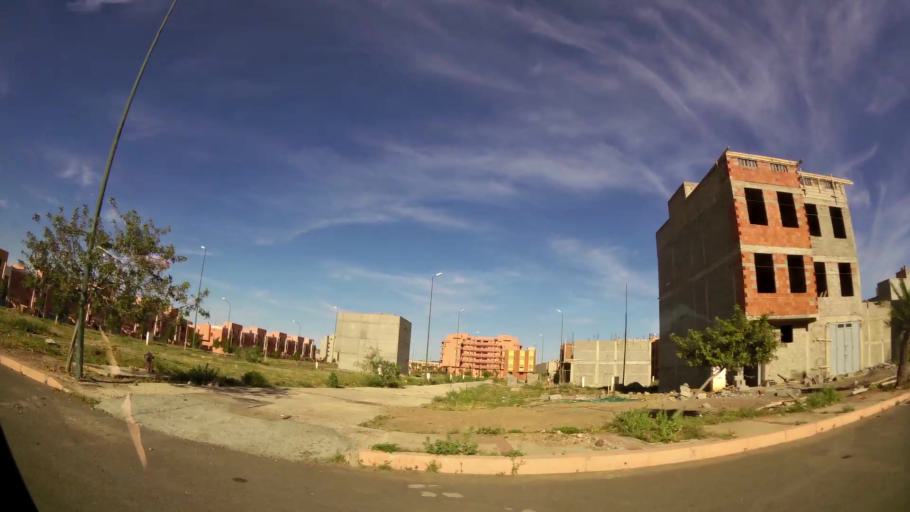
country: MA
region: Marrakech-Tensift-Al Haouz
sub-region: Marrakech
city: Marrakesh
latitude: 31.7535
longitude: -8.1053
